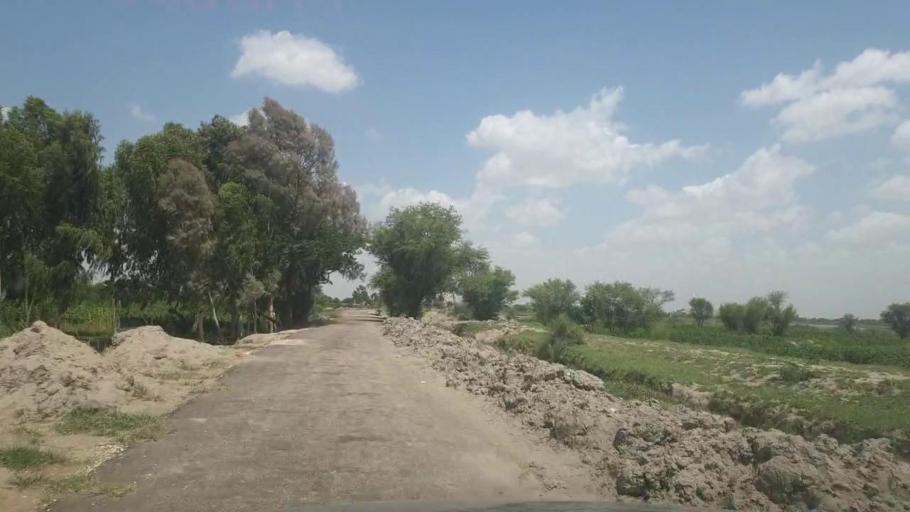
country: PK
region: Sindh
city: Kot Diji
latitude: 27.2357
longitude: 69.0303
